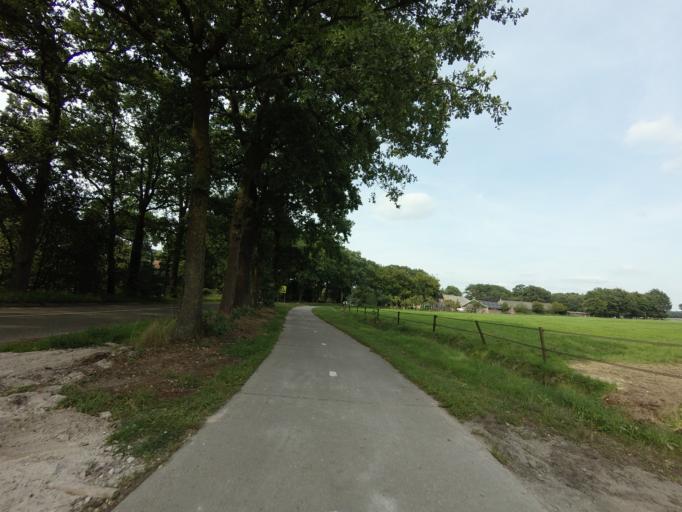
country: DE
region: Lower Saxony
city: Getelo
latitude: 52.4448
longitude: 6.8257
